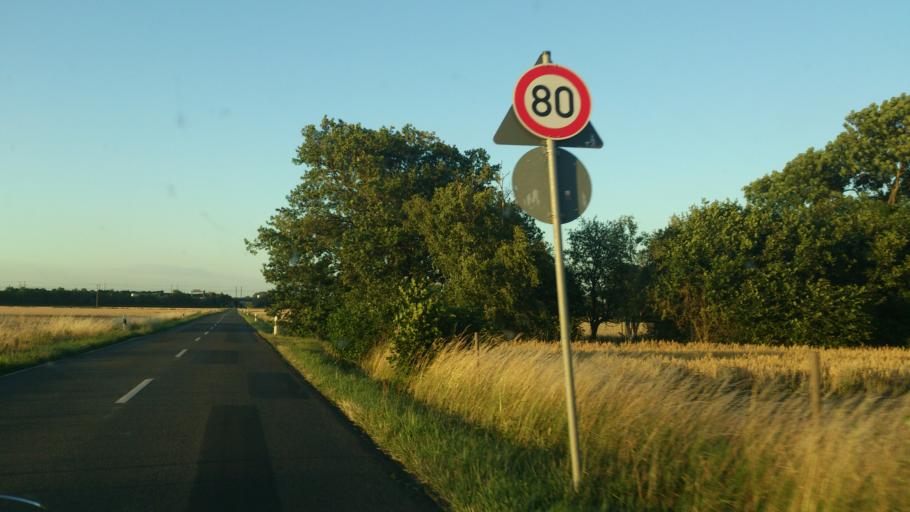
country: DE
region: Hesse
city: Raunheim
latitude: 50.0249
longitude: 8.4494
